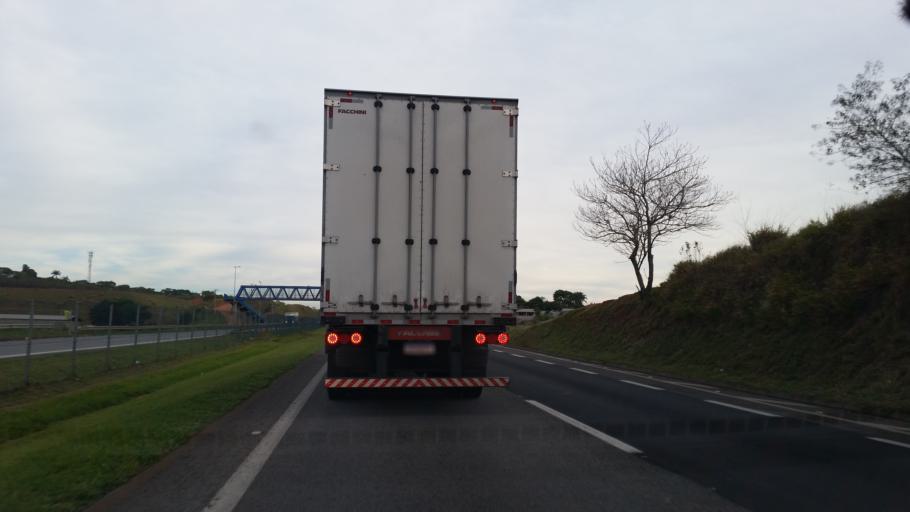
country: BR
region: Sao Paulo
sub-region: Atibaia
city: Atibaia
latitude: -23.0881
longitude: -46.6317
